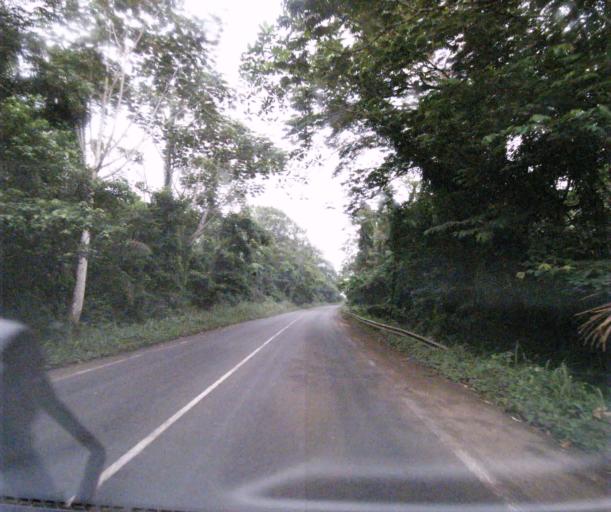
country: CM
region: Centre
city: Eseka
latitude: 3.8805
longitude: 10.6927
